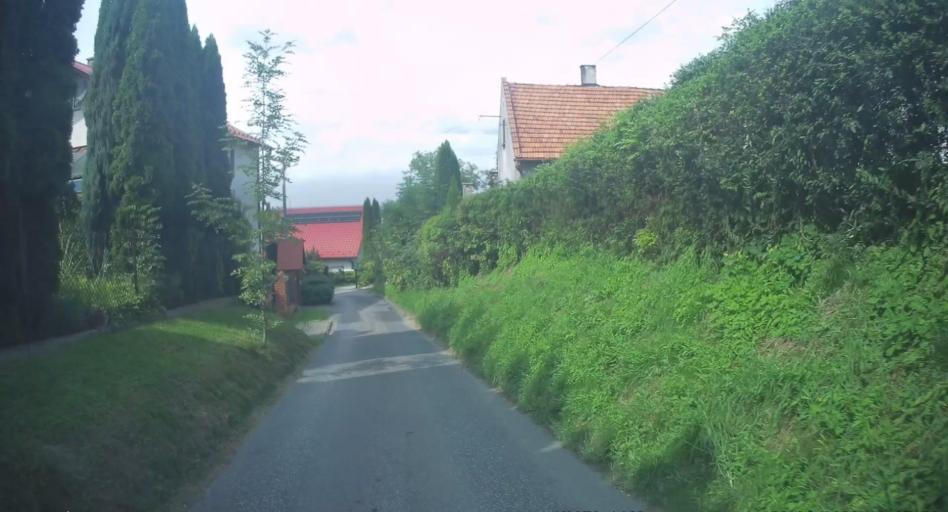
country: PL
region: Lesser Poland Voivodeship
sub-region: Powiat wielicki
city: Wieliczka
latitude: 49.9789
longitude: 20.0545
